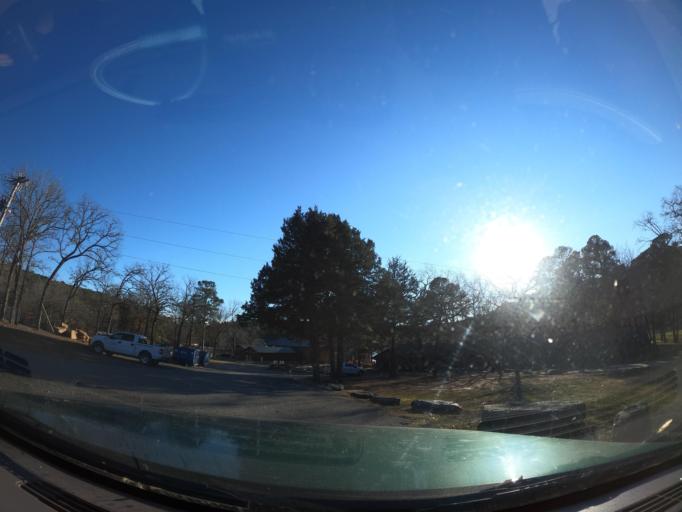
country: US
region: Oklahoma
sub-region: Latimer County
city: Wilburton
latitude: 34.9802
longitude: -95.3606
